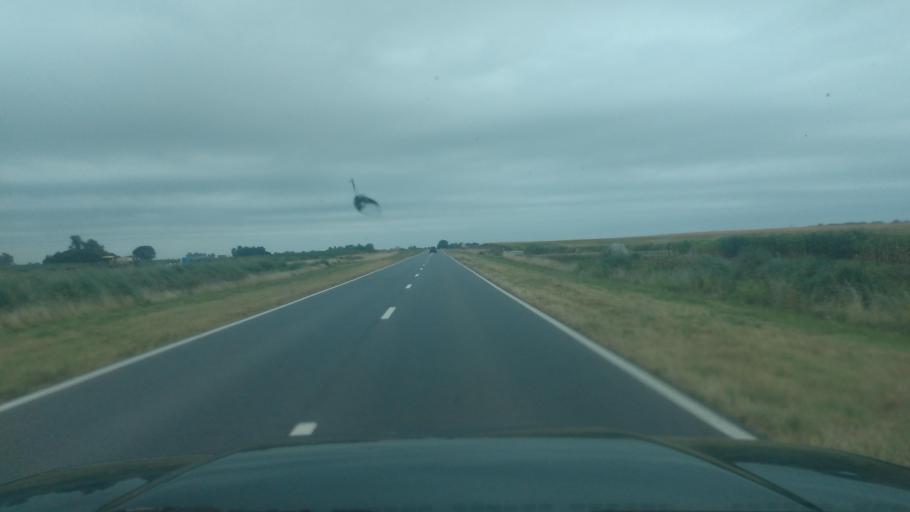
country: AR
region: Buenos Aires
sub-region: Partido de Bragado
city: Bragado
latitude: -35.3151
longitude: -60.6314
